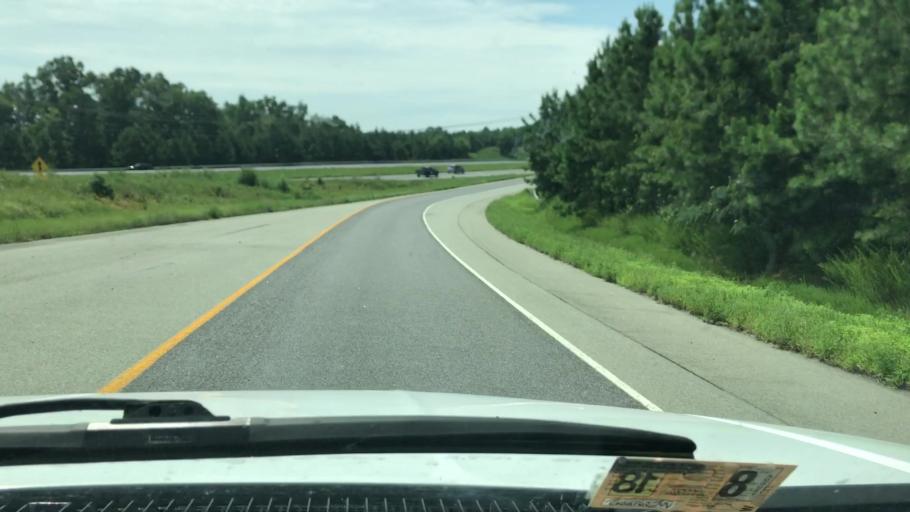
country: US
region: Virginia
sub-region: Henrico County
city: Short Pump
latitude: 37.5965
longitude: -77.6688
